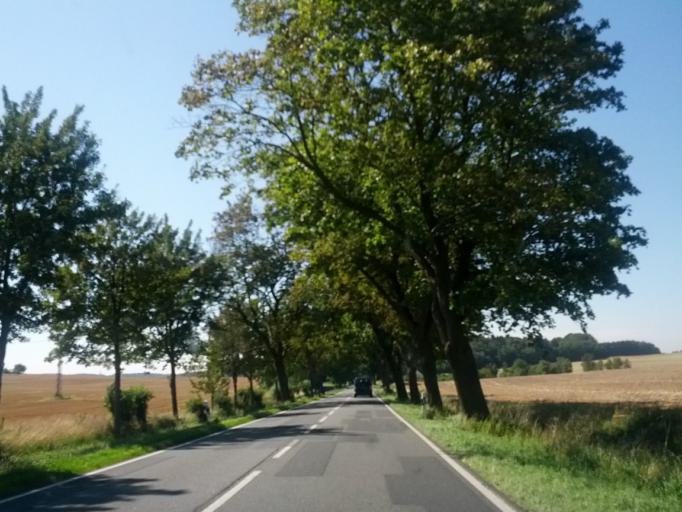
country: DE
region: Mecklenburg-Vorpommern
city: Bergen auf Ruegen
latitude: 54.4540
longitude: 13.4437
